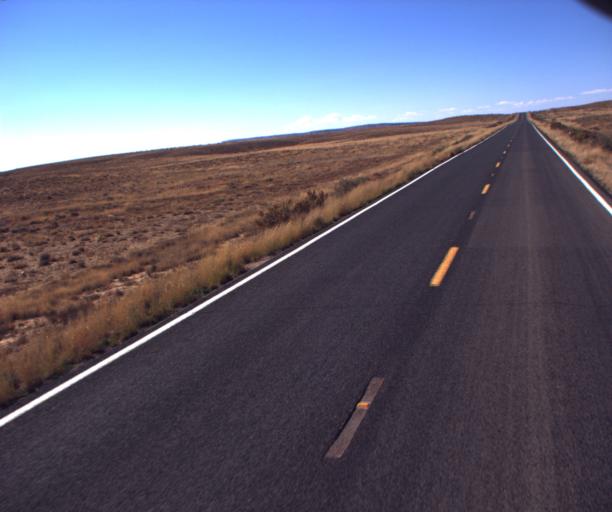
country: US
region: Arizona
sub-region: Navajo County
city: First Mesa
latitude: 35.9779
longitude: -110.7483
